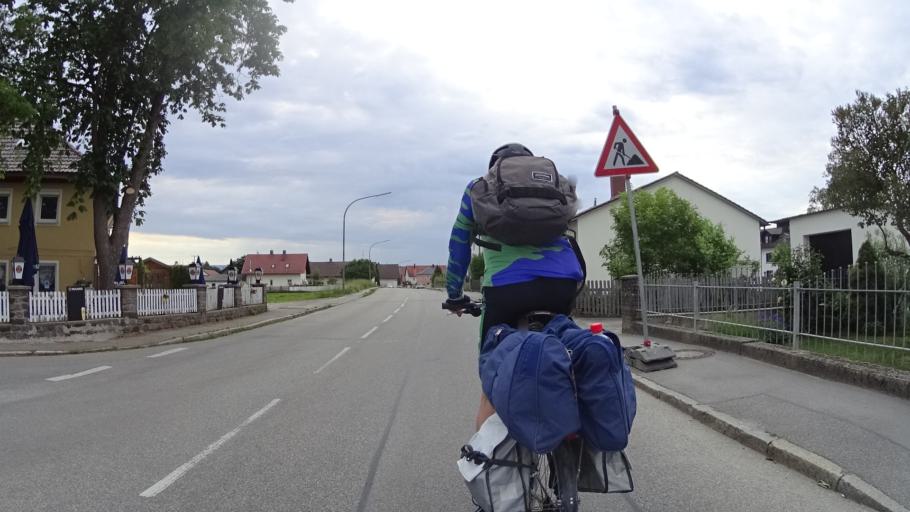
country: DE
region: Bavaria
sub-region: Lower Bavaria
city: Parkstetten
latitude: 48.9163
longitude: 12.6031
